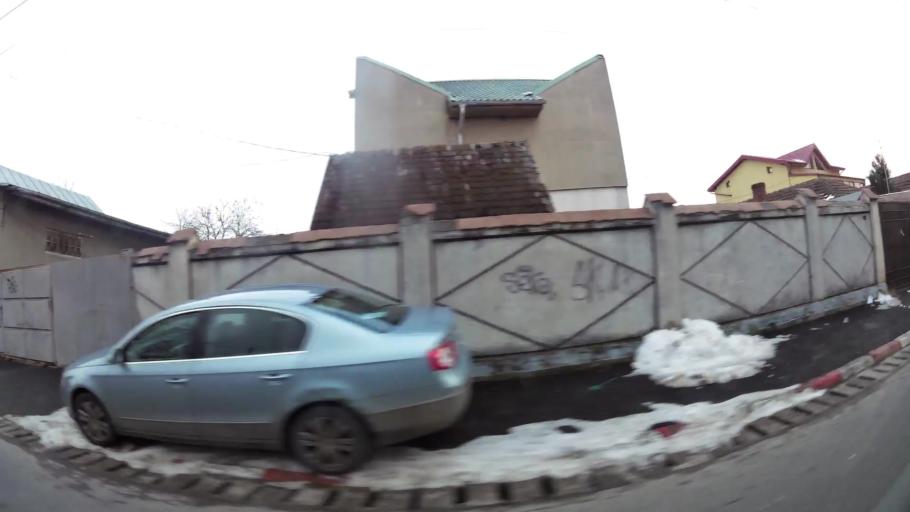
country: RO
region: Ilfov
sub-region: Voluntari City
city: Voluntari
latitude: 44.4823
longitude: 26.1820
